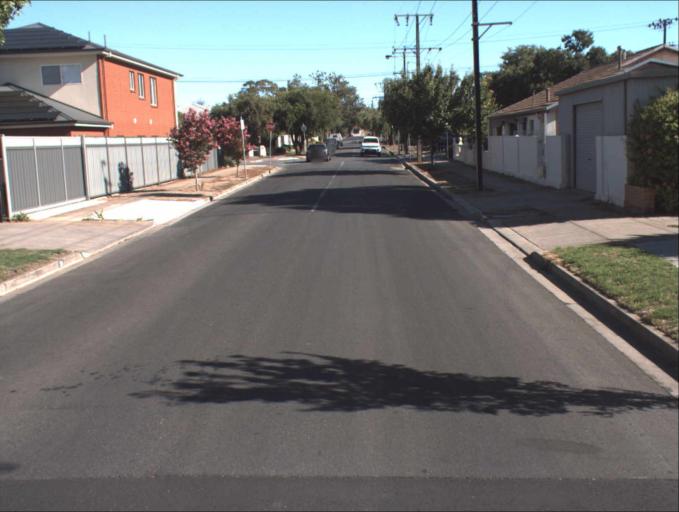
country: AU
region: South Australia
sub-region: Prospect
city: Prospect
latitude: -34.8769
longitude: 138.6109
